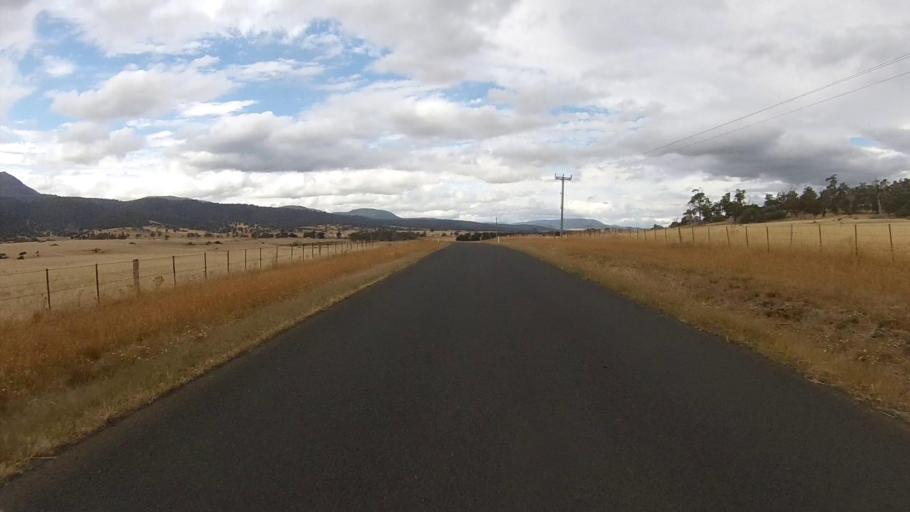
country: AU
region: Tasmania
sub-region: Northern Midlands
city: Evandale
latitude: -41.8249
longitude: 147.8089
